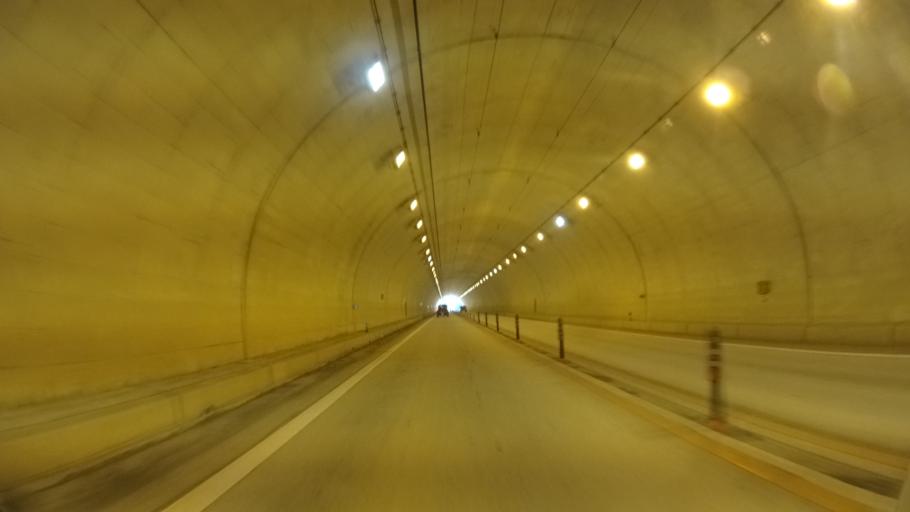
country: JP
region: Yamaguchi
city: Hagi
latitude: 34.3820
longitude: 131.3111
